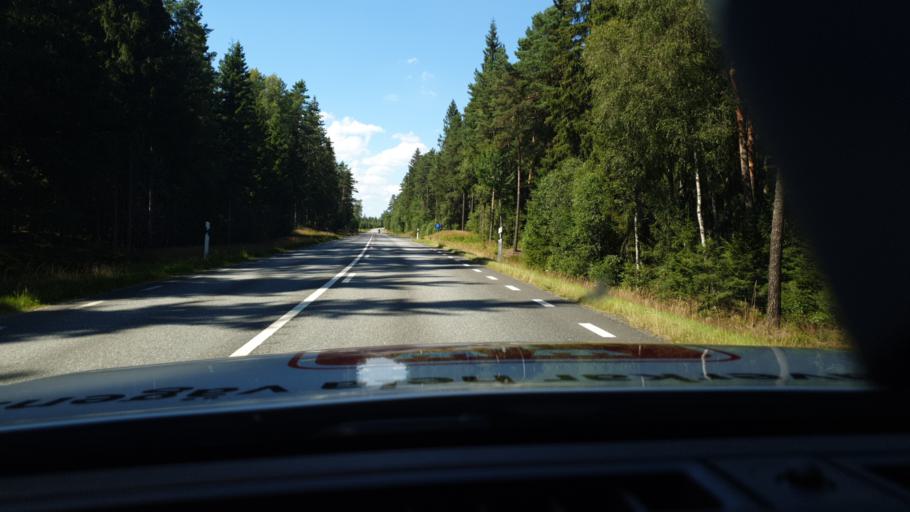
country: SE
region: Joenkoeping
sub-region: Savsjo Kommun
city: Vrigstad
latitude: 57.3862
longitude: 14.3954
